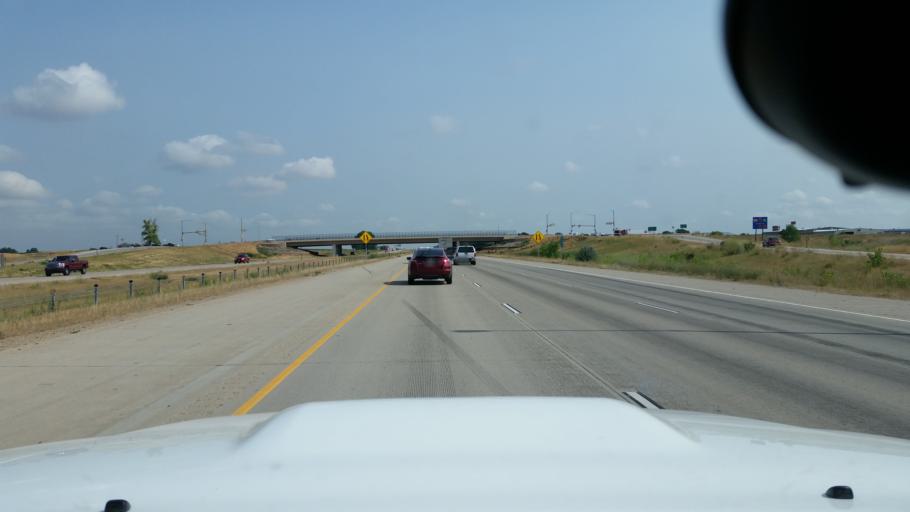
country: US
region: Colorado
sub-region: Weld County
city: Mead
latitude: 40.2007
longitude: -104.9800
